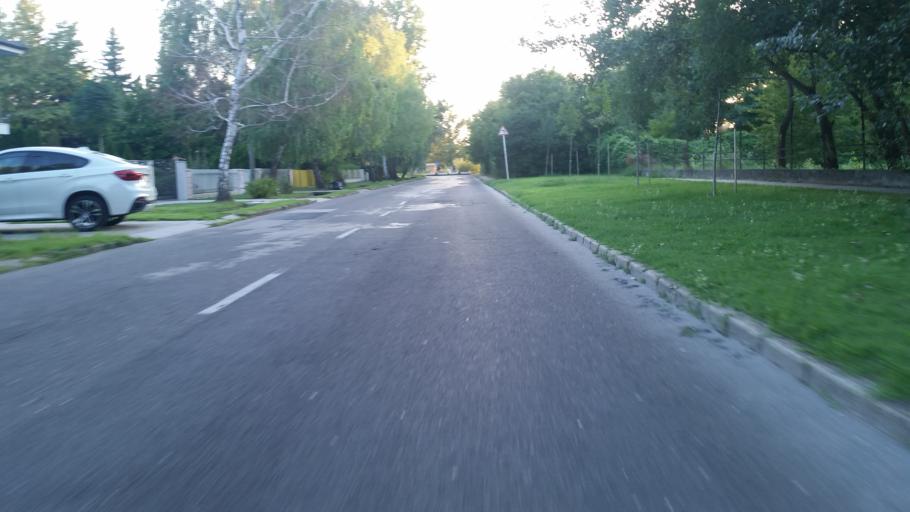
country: HU
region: Somogy
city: Siofok
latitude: 46.8988
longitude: 18.0065
